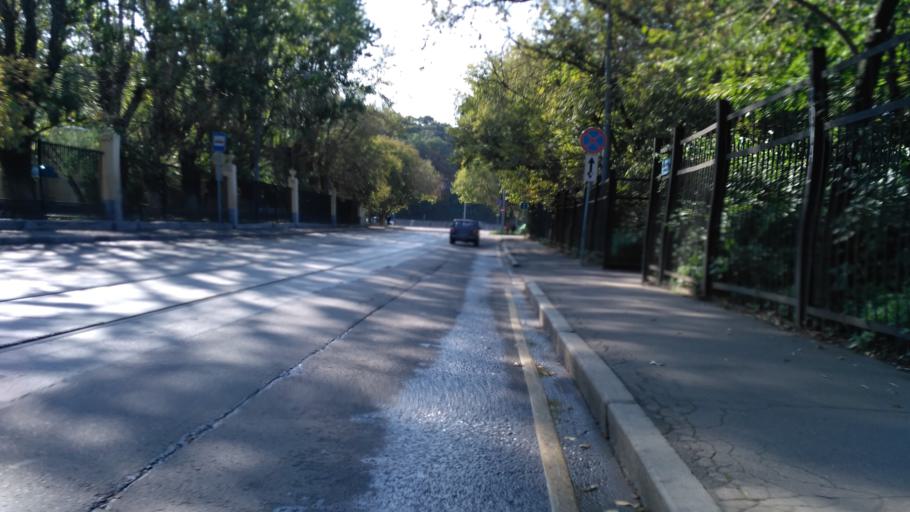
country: RU
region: Moscow
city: Lefortovo
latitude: 55.7608
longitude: 37.6730
